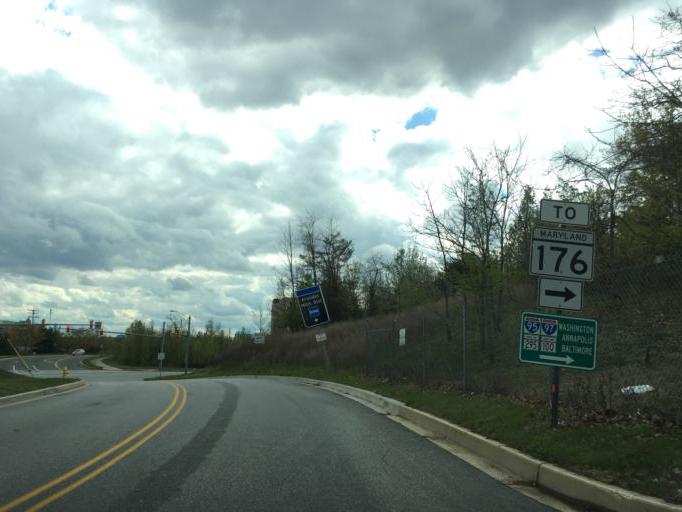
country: US
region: Maryland
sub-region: Anne Arundel County
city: Severn
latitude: 39.1633
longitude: -76.7117
